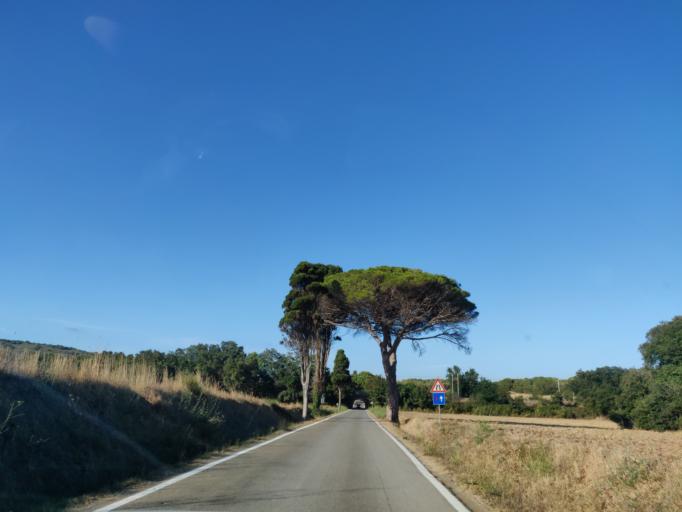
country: IT
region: Tuscany
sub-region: Provincia di Grosseto
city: Orbetello Scalo
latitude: 42.4124
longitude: 11.2968
